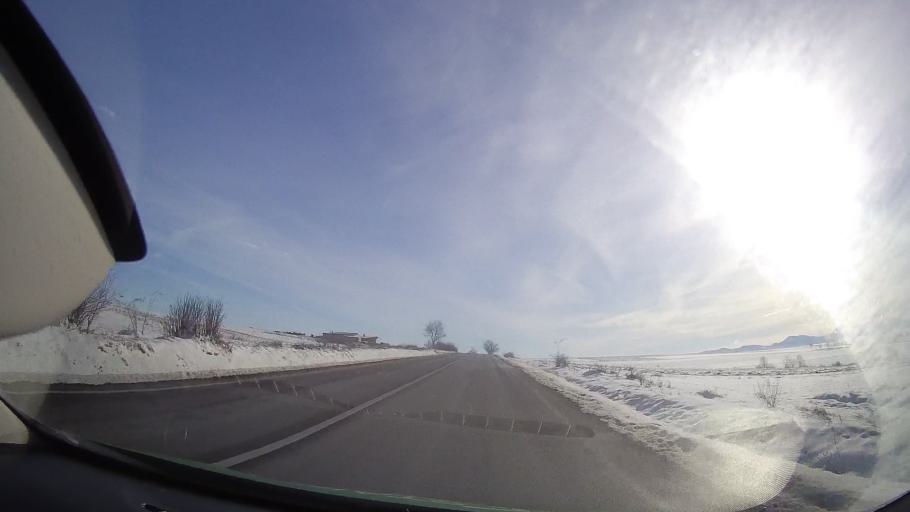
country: RO
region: Neamt
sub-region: Comuna Baltatesti
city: Valea Seaca
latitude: 47.1605
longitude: 26.3192
